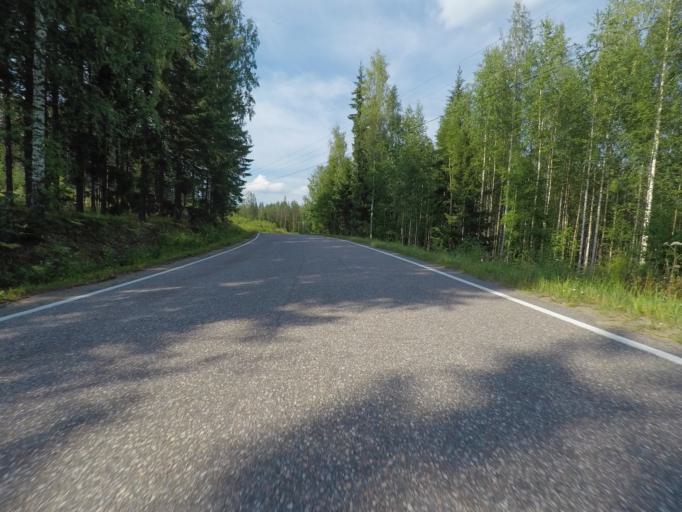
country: FI
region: Southern Savonia
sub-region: Savonlinna
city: Sulkava
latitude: 61.7774
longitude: 28.2394
